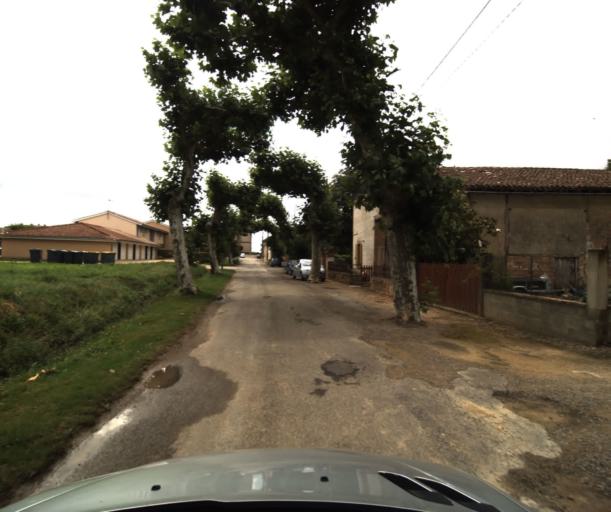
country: FR
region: Midi-Pyrenees
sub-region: Departement du Tarn-et-Garonne
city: Lavit
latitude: 43.9597
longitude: 0.9196
